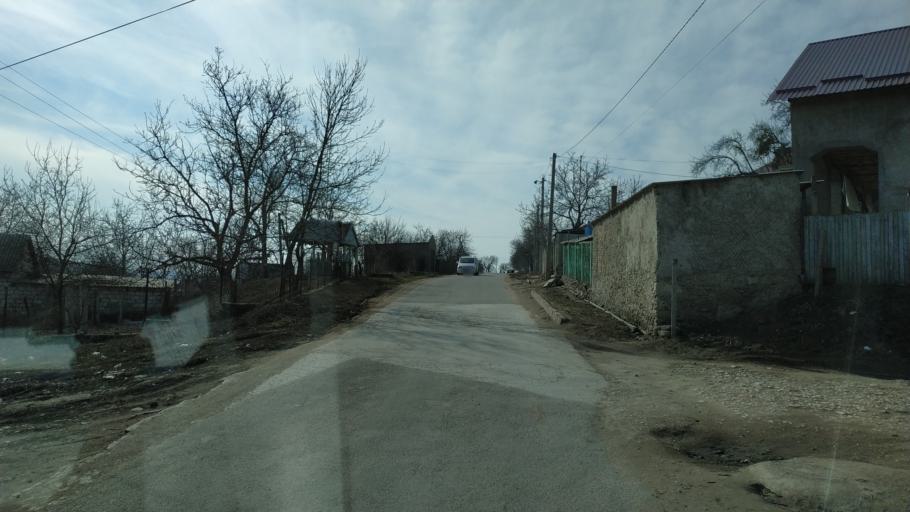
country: MD
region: Nisporeni
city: Nisporeni
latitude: 47.1537
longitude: 28.1306
